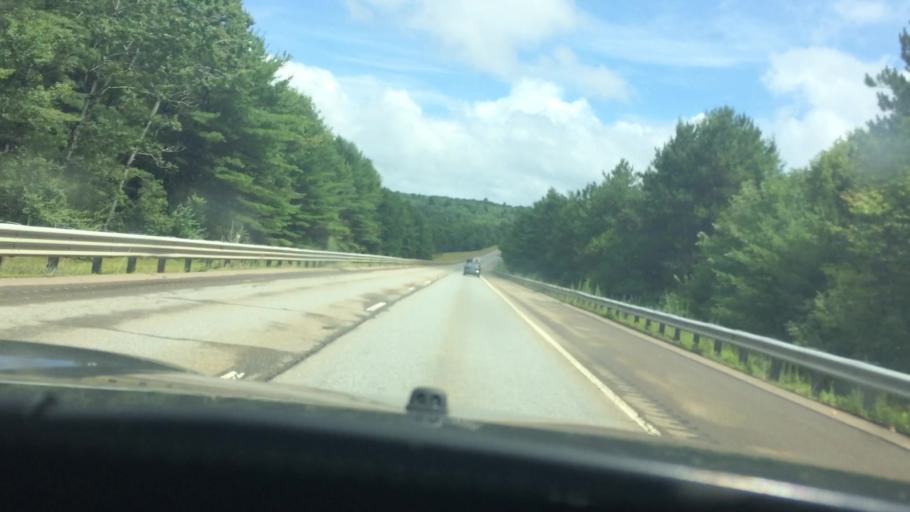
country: US
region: Massachusetts
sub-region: Worcester County
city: Templeton
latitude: 42.5690
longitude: -72.0932
